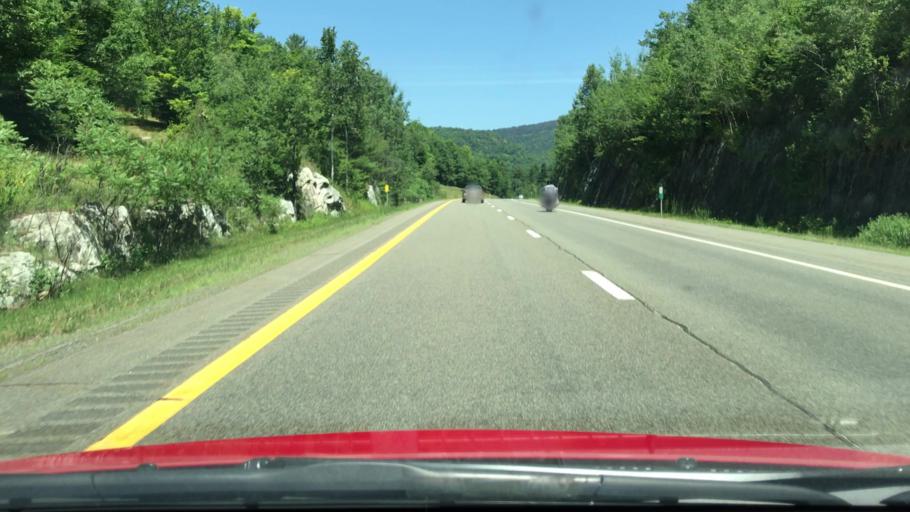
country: US
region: New York
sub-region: Essex County
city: Keeseville
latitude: 44.3651
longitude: -73.5293
